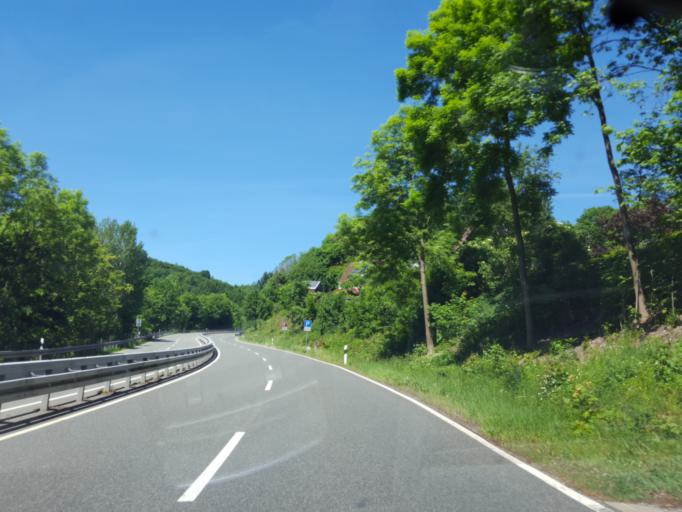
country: DE
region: Lower Saxony
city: Osterode am Harz
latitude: 51.7499
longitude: 10.2873
